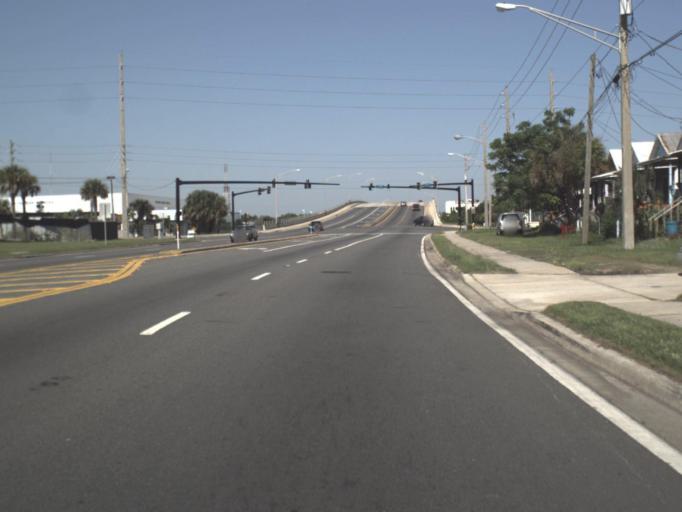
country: US
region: Florida
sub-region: Duval County
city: Jacksonville
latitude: 30.3357
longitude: -81.6817
